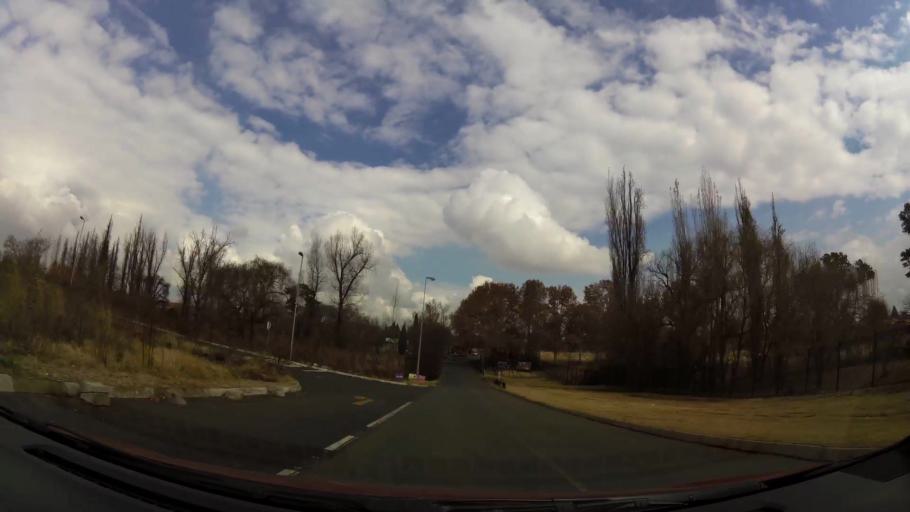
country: ZA
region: Gauteng
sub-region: Sedibeng District Municipality
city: Vanderbijlpark
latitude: -26.7417
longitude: 27.8428
